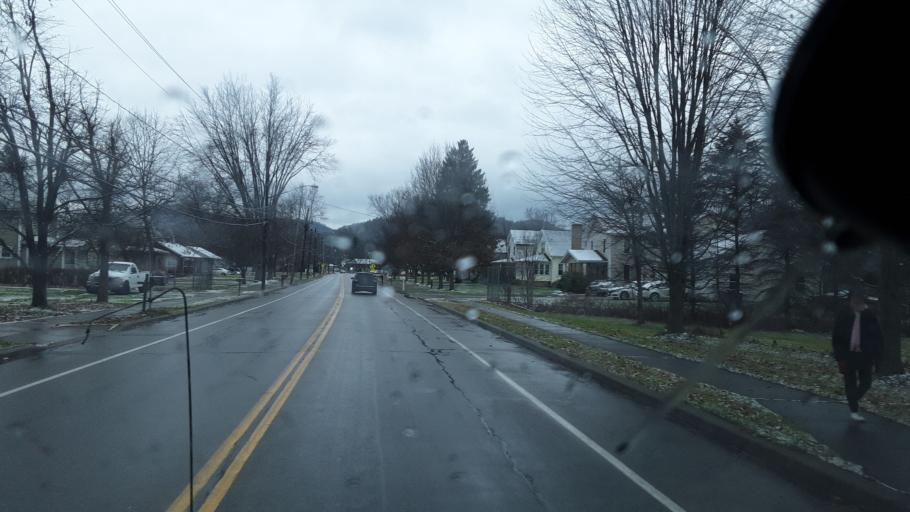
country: US
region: New York
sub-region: Cattaraugus County
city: Portville
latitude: 42.0313
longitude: -78.3379
